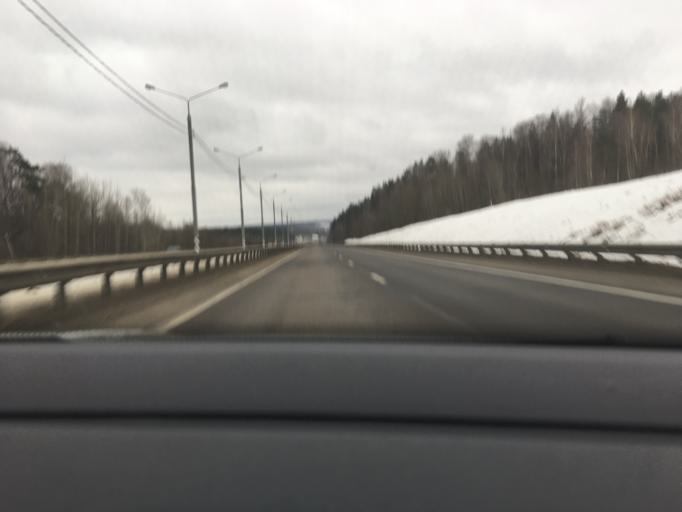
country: RU
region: Tula
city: Zaokskiy
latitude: 54.7874
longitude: 37.4872
